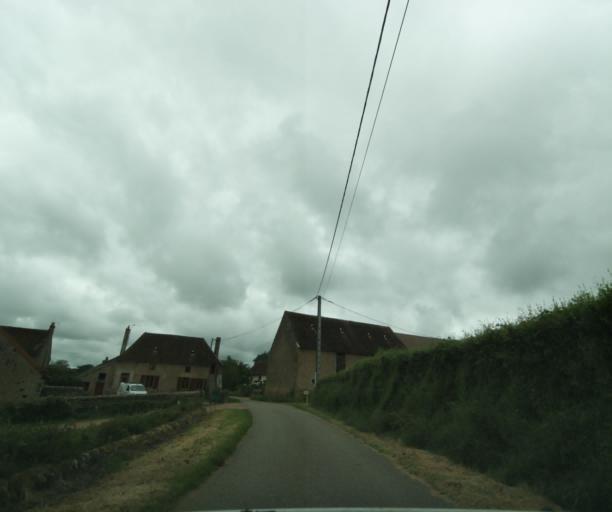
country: FR
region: Bourgogne
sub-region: Departement de Saone-et-Loire
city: Charolles
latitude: 46.4827
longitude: 4.3228
